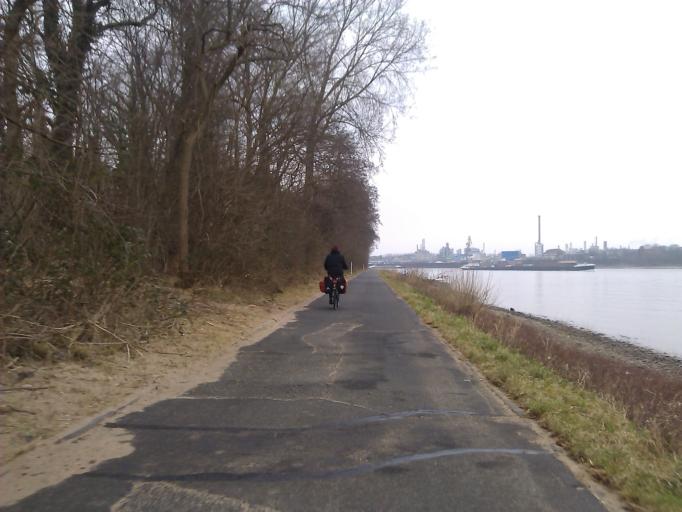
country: DE
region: North Rhine-Westphalia
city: Niederkassel
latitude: 50.8145
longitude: 7.0246
